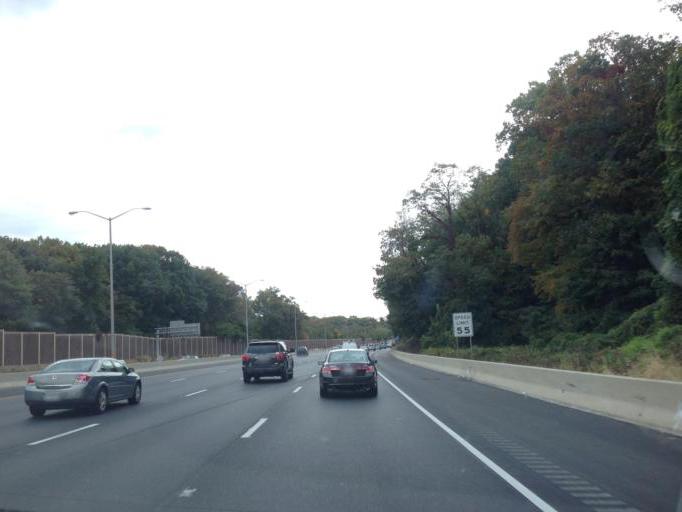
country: US
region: Maryland
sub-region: Baltimore County
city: Pikesville
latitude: 39.3945
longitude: -76.7003
